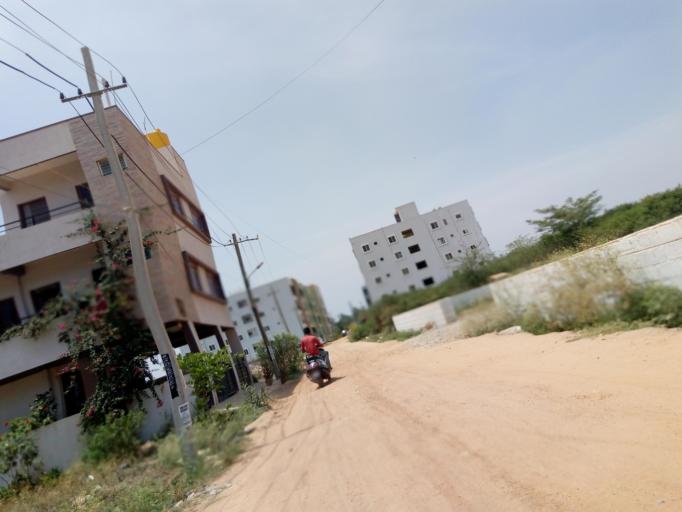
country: IN
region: Karnataka
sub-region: Bangalore Urban
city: Bangalore
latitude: 12.8861
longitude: 77.6602
